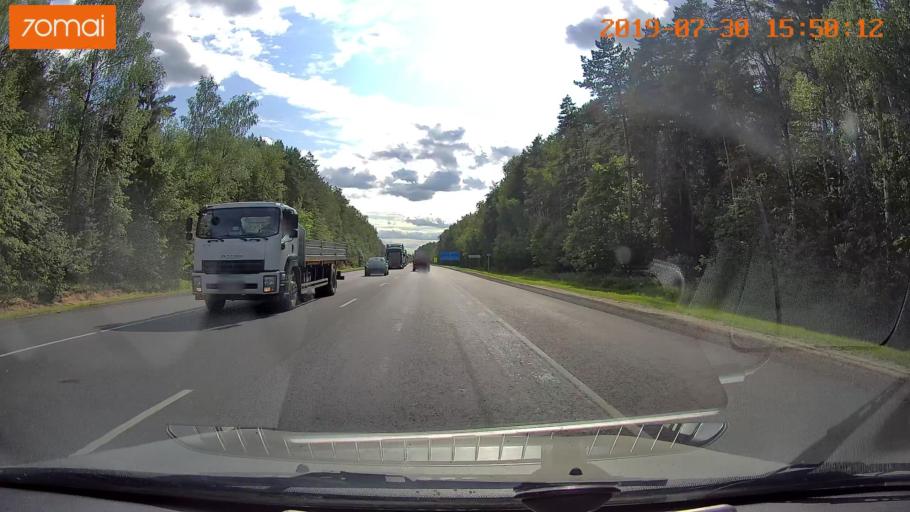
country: RU
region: Moskovskaya
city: Voskresensk
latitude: 55.3329
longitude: 38.6548
